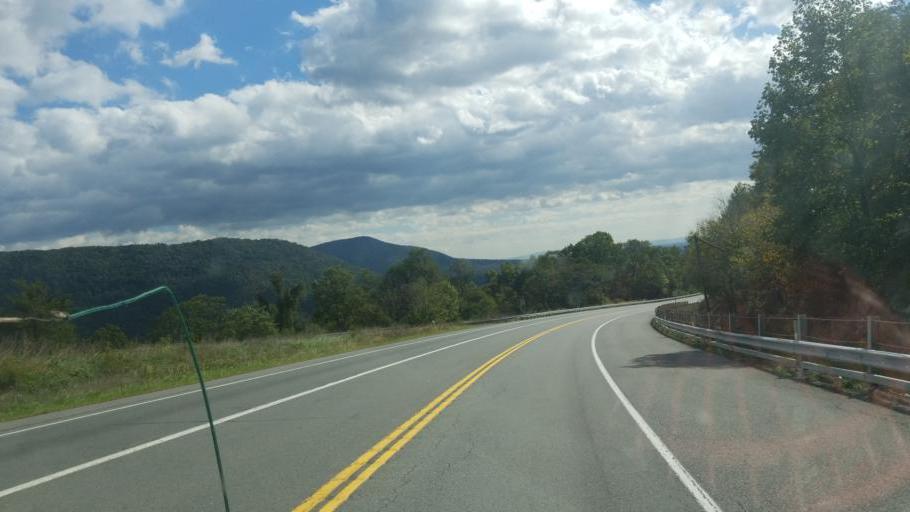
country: US
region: Pennsylvania
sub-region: Fulton County
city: McConnellsburg
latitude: 39.9361
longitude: -77.9217
